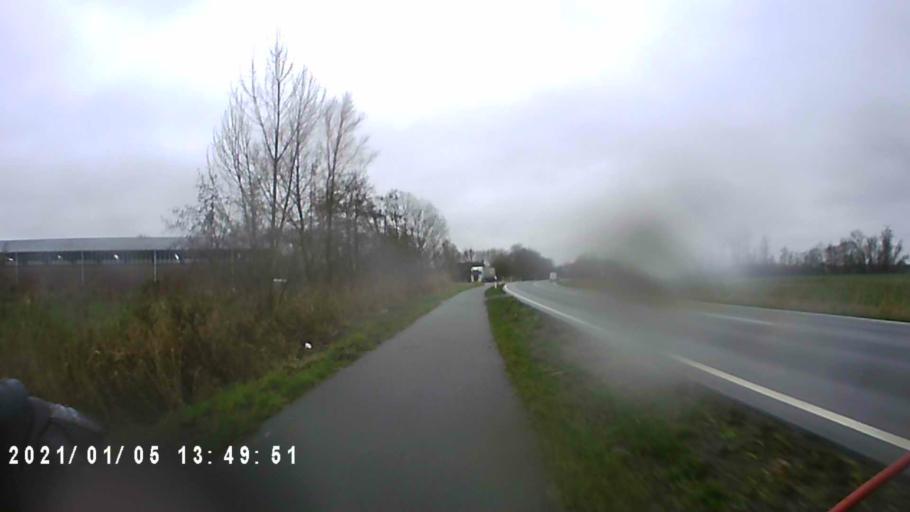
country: DE
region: Lower Saxony
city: Weener
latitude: 53.1754
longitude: 7.3689
